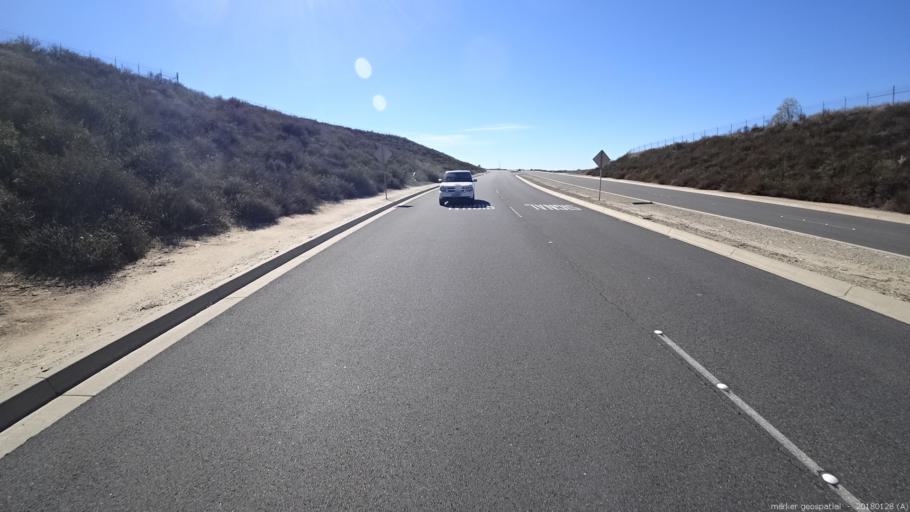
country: US
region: California
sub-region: San Bernardino County
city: Chino Hills
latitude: 34.0125
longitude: -117.7691
